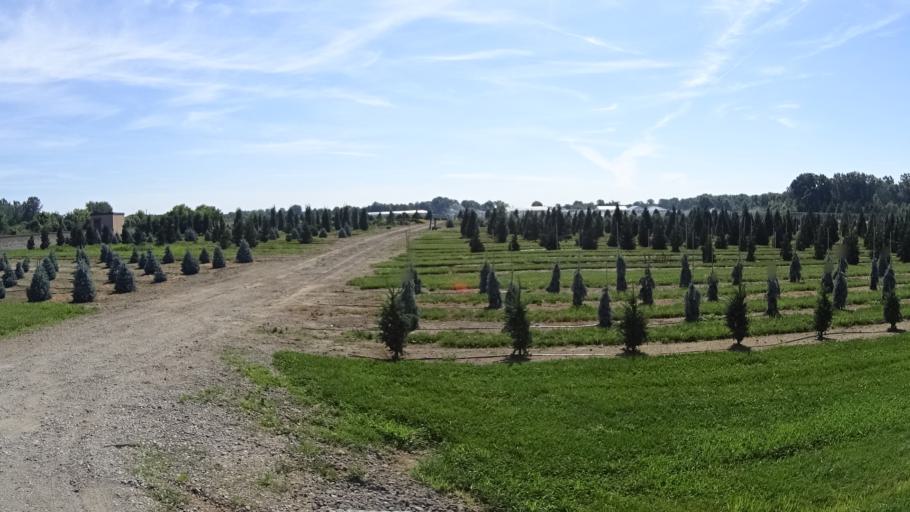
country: US
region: Ohio
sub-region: Erie County
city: Huron
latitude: 41.3757
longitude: -82.4720
